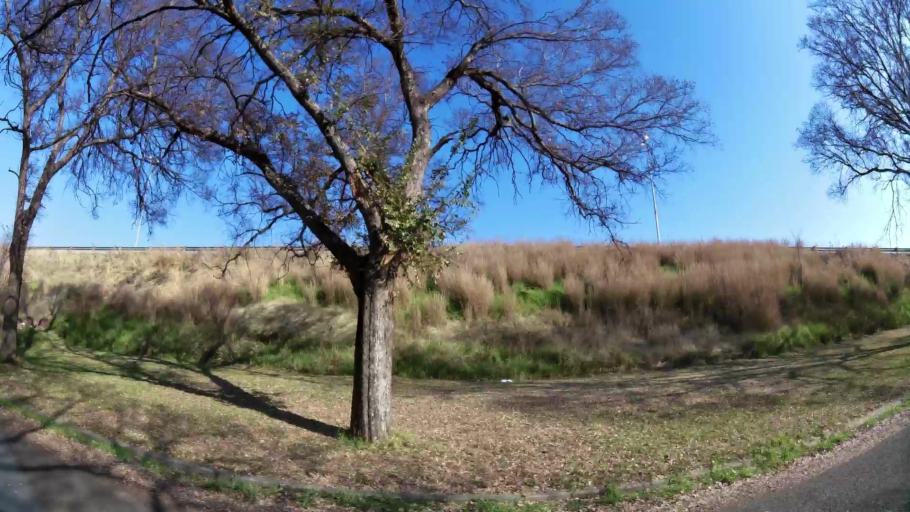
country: ZA
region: Gauteng
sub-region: Ekurhuleni Metropolitan Municipality
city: Boksburg
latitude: -26.2180
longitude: 28.2355
